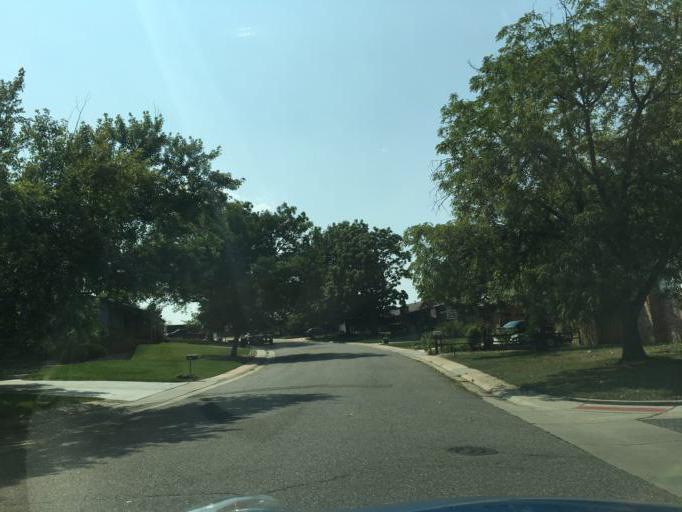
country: US
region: Colorado
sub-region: Jefferson County
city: Arvada
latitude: 39.8369
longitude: -105.0778
